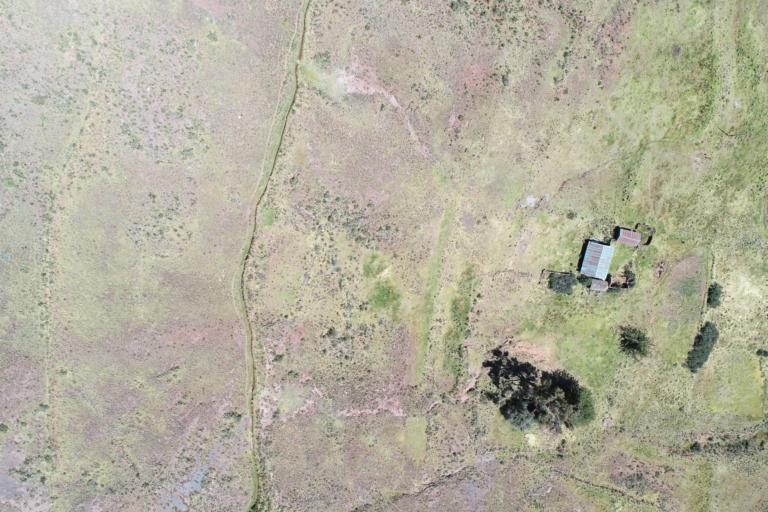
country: BO
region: La Paz
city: Tiahuanaco
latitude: -16.6092
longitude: -68.7623
